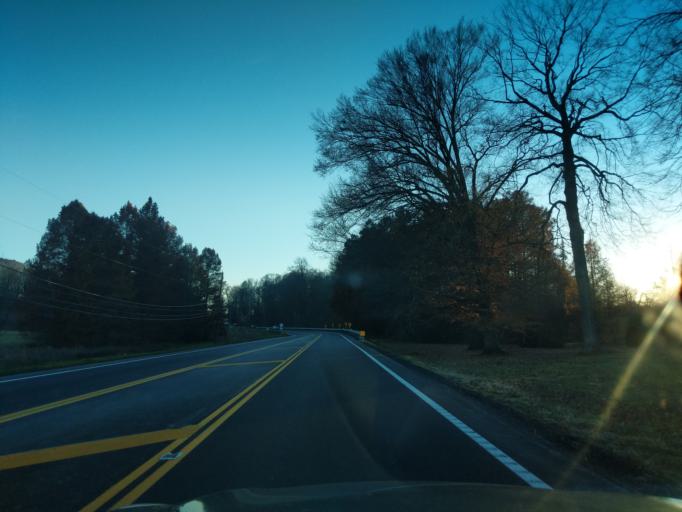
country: US
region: Ohio
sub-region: Licking County
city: Harbor Hills
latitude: 39.9795
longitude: -82.4110
